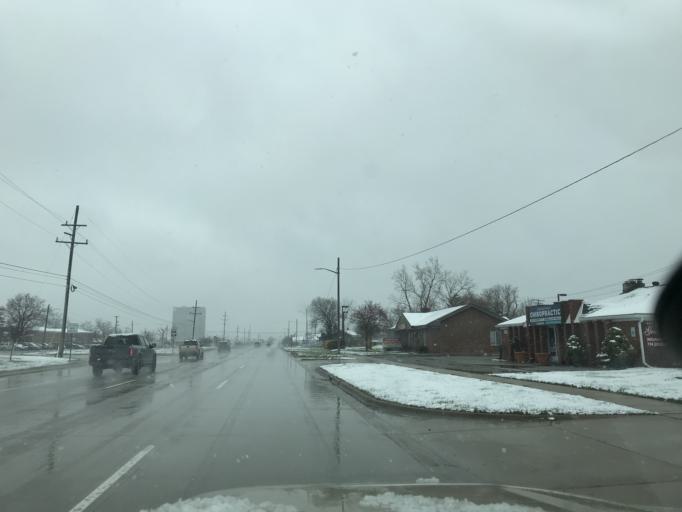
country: US
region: Michigan
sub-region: Wayne County
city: Riverview
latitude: 42.1800
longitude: -83.1891
